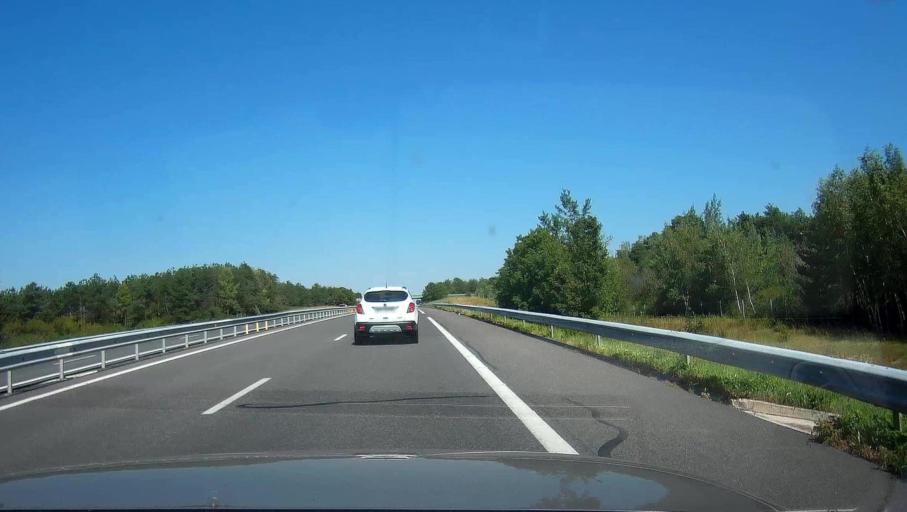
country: FR
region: Champagne-Ardenne
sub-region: Departement de l'Aube
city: Arcis-sur-Aube
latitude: 48.4886
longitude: 4.1644
